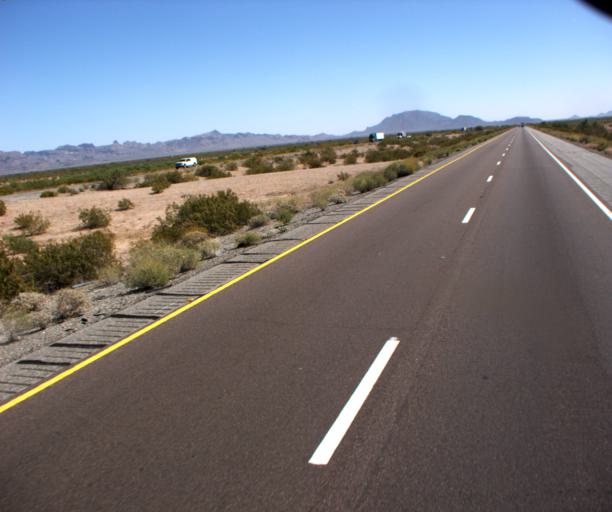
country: US
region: Arizona
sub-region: La Paz County
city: Salome
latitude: 33.5511
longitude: -113.2371
